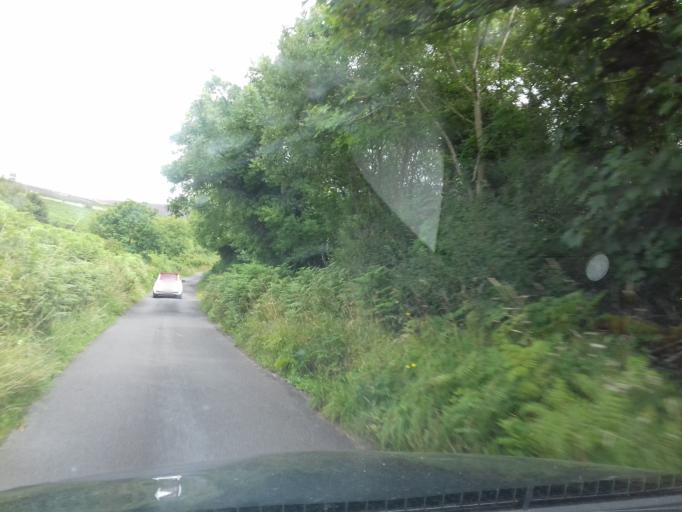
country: IE
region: Leinster
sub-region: County Carlow
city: Bagenalstown
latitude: 52.6267
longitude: -6.8229
